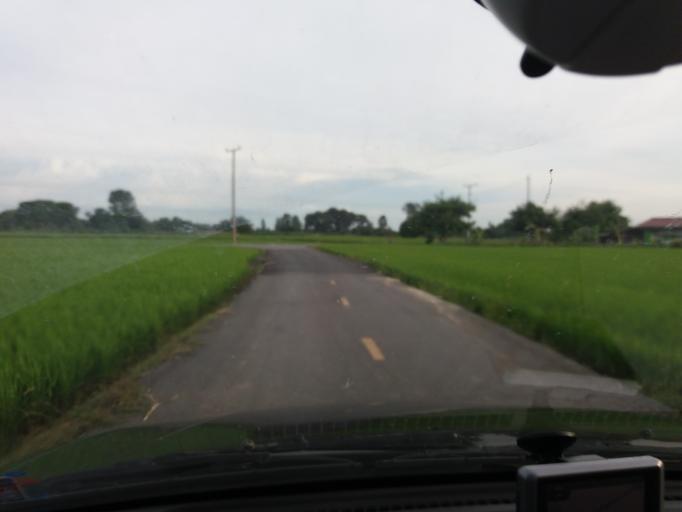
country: TH
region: Suphan Buri
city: Doembang Nangbuat
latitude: 14.8245
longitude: 100.1420
